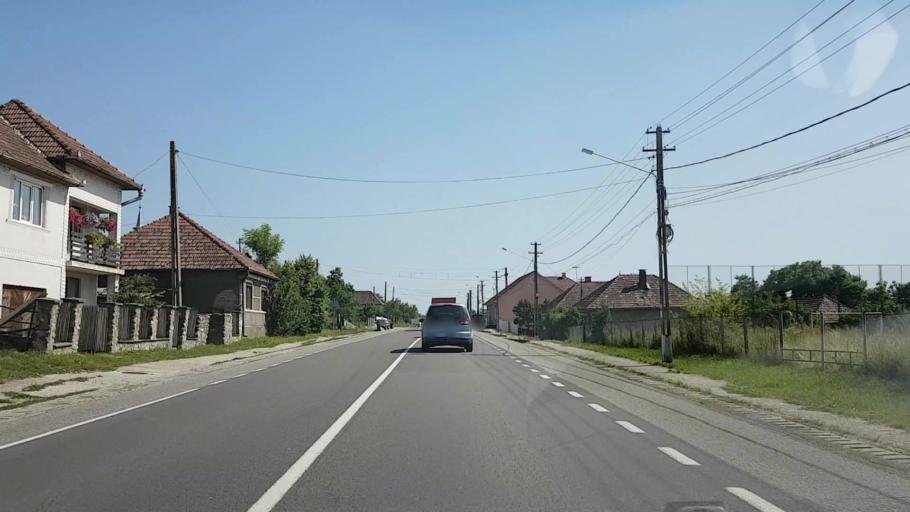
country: RO
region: Bistrita-Nasaud
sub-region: Comuna Sieu-Odorhei
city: Sieu-Odorhei
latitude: 47.1458
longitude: 24.3063
